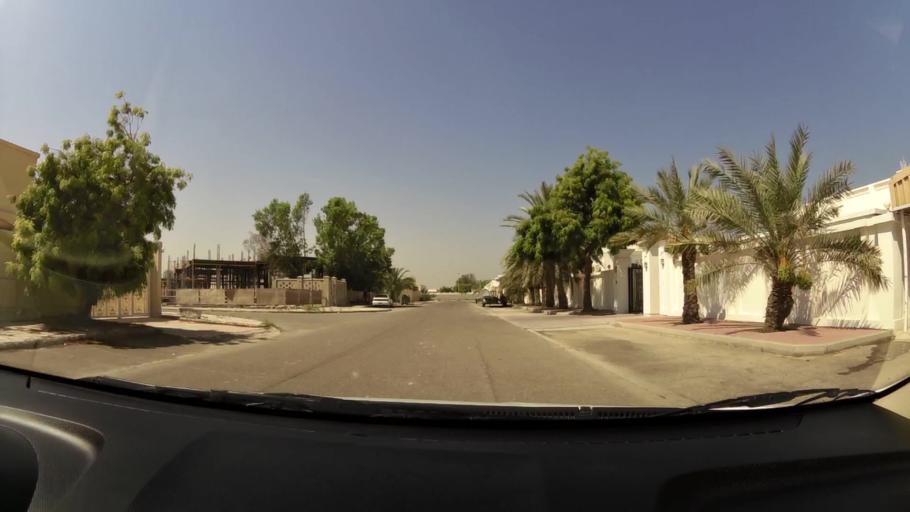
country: AE
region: Umm al Qaywayn
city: Umm al Qaywayn
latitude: 25.5575
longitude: 55.5456
